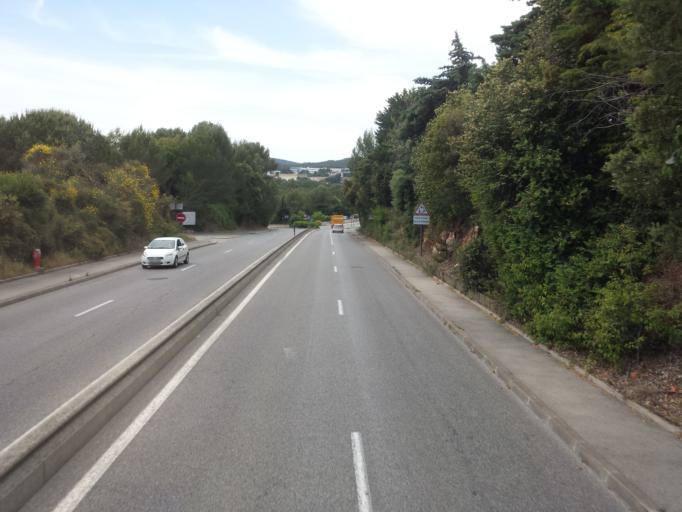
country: FR
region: Provence-Alpes-Cote d'Azur
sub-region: Departement des Alpes-Maritimes
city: Biot
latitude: 43.6135
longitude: 7.0796
